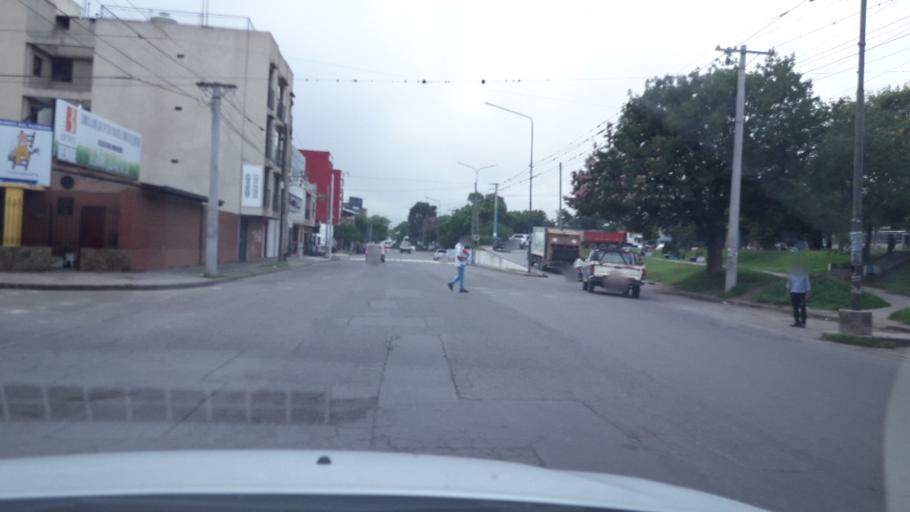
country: AR
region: Jujuy
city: San Salvador de Jujuy
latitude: -24.1962
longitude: -65.2907
